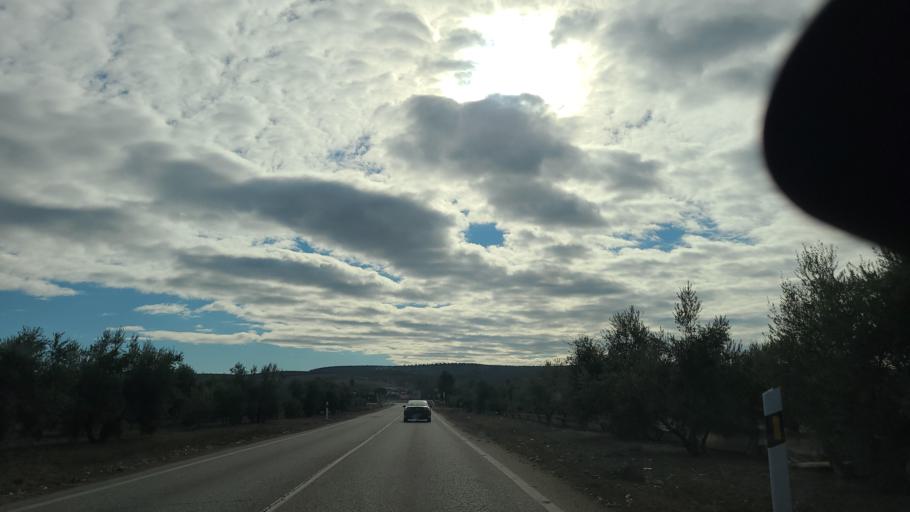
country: ES
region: Andalusia
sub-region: Provincia de Jaen
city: Villanueva de la Reina
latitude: 38.0127
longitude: -3.9128
